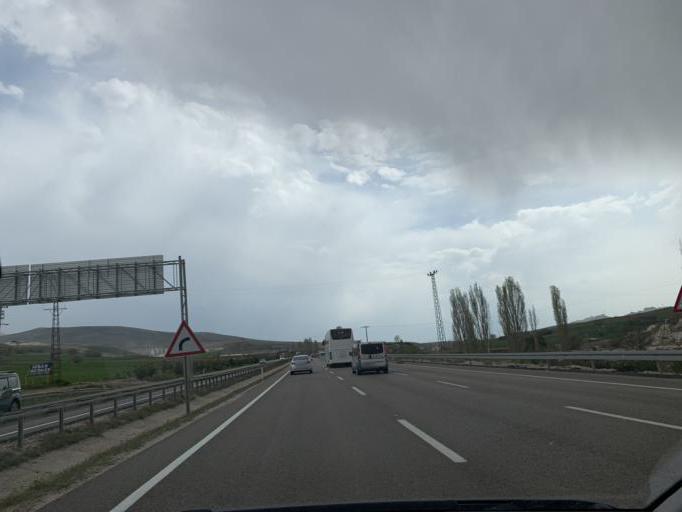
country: TR
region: Eskisehir
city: Sivrihisar
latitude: 39.4896
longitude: 31.6002
